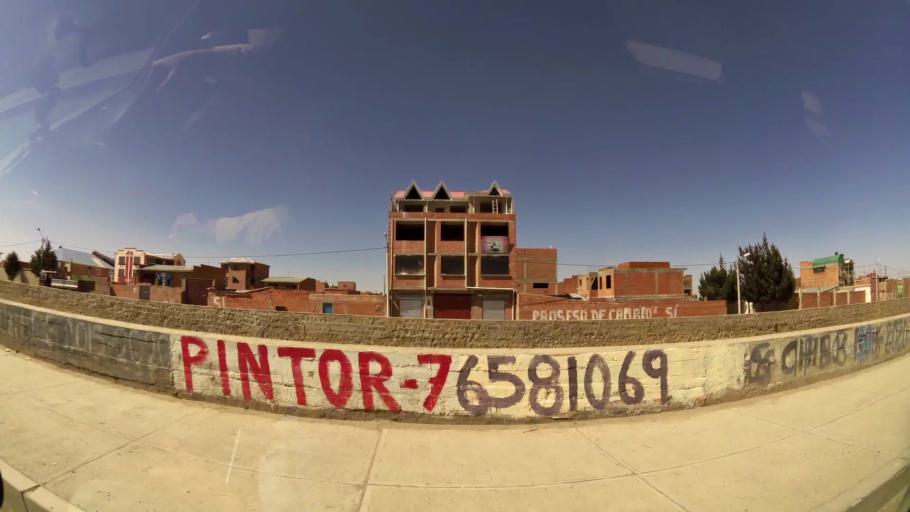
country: BO
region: La Paz
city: La Paz
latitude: -16.5169
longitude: -68.2211
